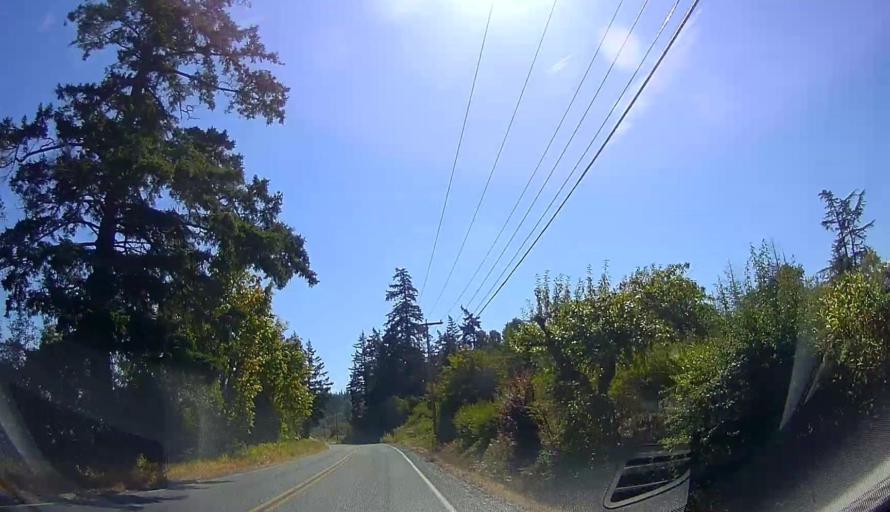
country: US
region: Washington
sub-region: Skagit County
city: Anacortes
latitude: 48.4705
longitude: -122.5408
